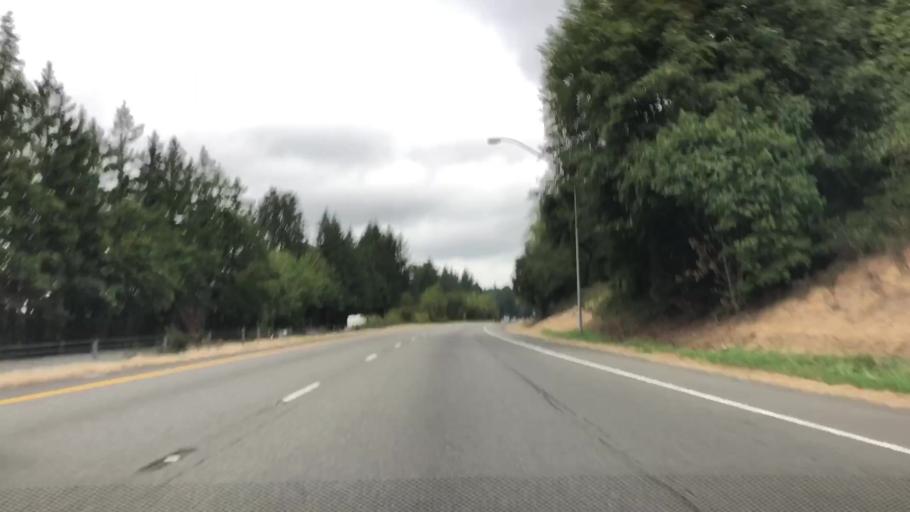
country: US
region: Washington
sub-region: Kitsap County
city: Burley
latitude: 47.4102
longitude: -122.6246
